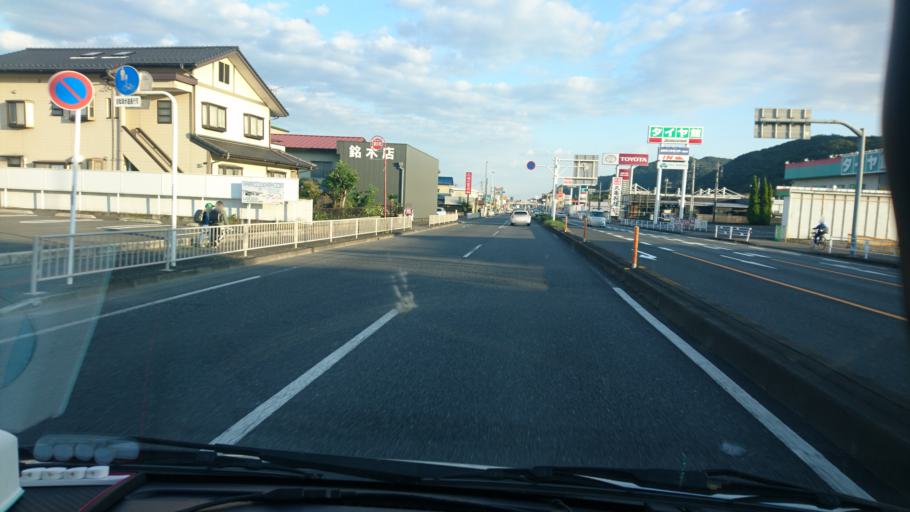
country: JP
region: Gunma
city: Kiryu
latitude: 36.3804
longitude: 139.3421
